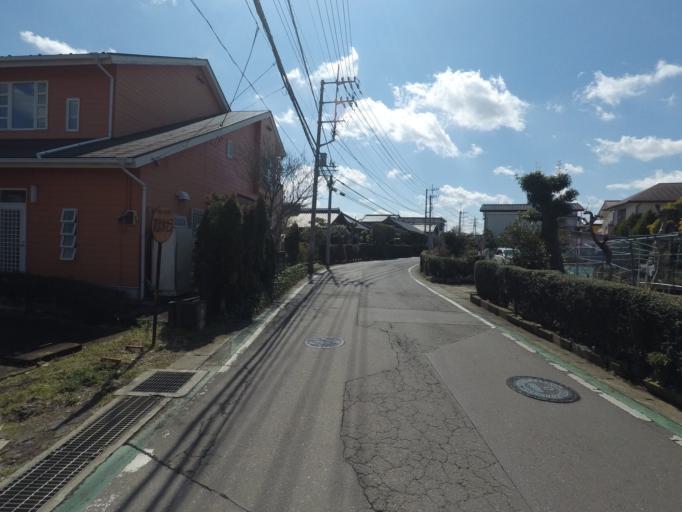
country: JP
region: Ibaraki
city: Naka
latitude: 36.0547
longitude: 140.1147
